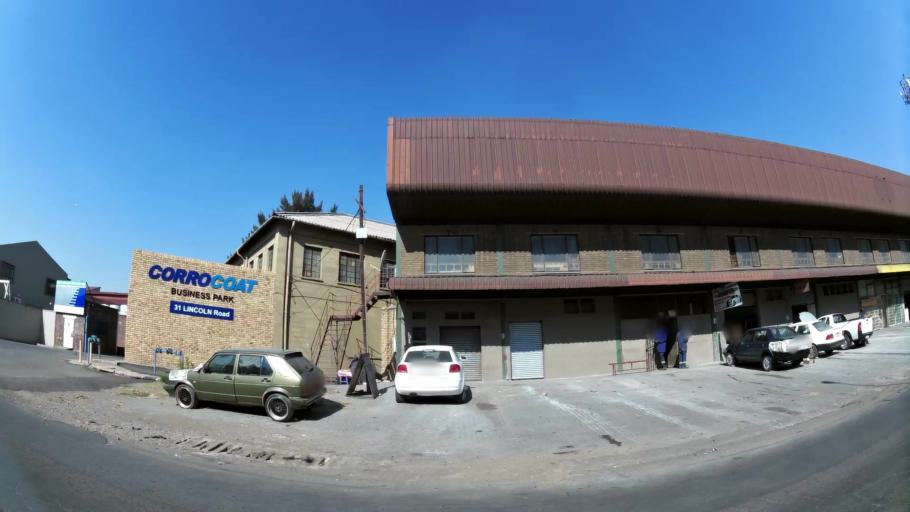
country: ZA
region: Gauteng
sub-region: Ekurhuleni Metropolitan Municipality
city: Benoni
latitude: -26.2075
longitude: 28.2957
